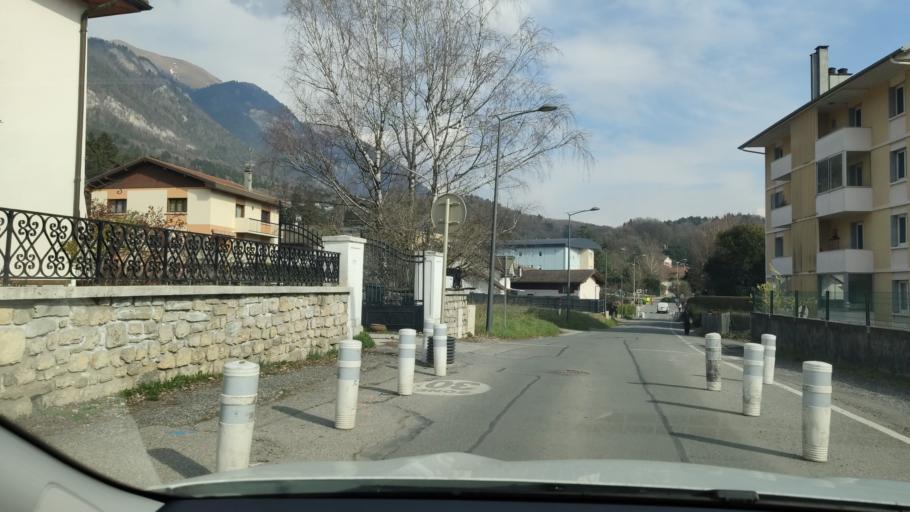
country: FR
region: Rhone-Alpes
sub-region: Departement de la Haute-Savoie
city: Bonneville
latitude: 46.0849
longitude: 6.4075
